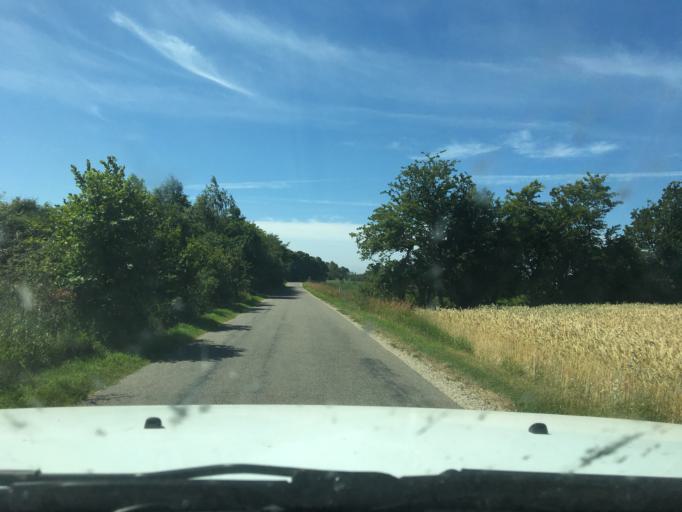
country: DK
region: Central Jutland
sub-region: Viborg Kommune
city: Bjerringbro
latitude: 56.5281
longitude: 9.6691
